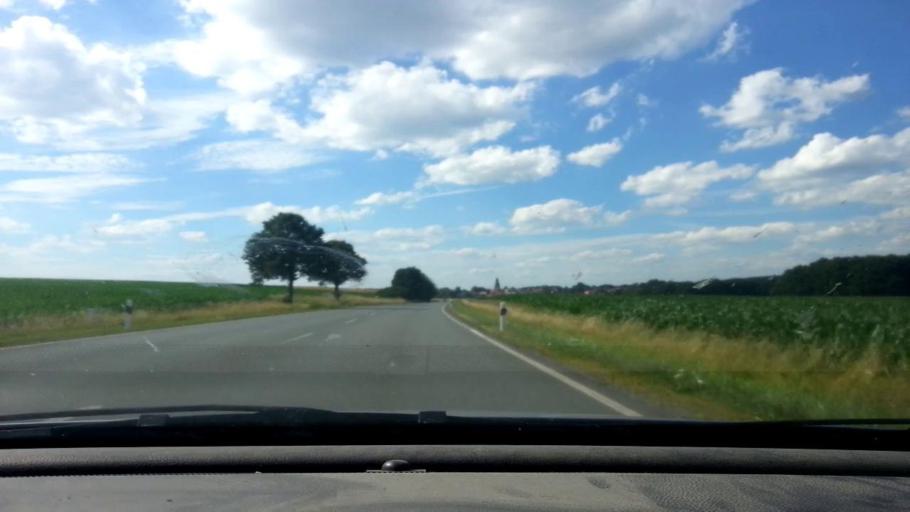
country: DE
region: Bavaria
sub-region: Upper Franconia
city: Neunkirchen am Main
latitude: 49.9124
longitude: 11.6567
